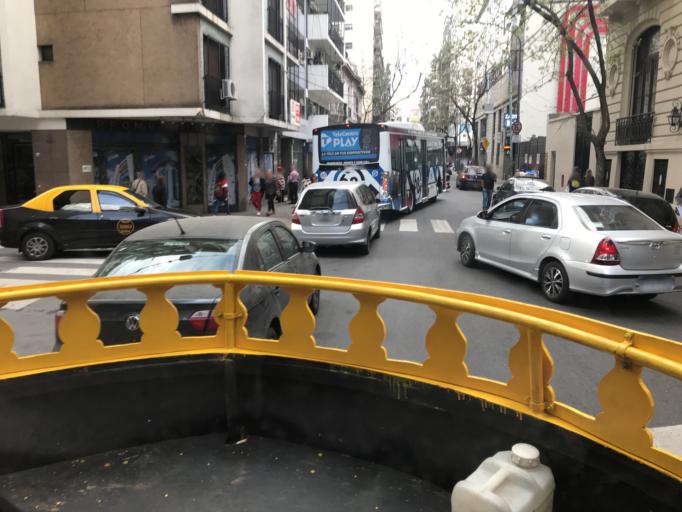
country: AR
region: Buenos Aires F.D.
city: Retiro
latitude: -34.5970
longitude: -58.4019
